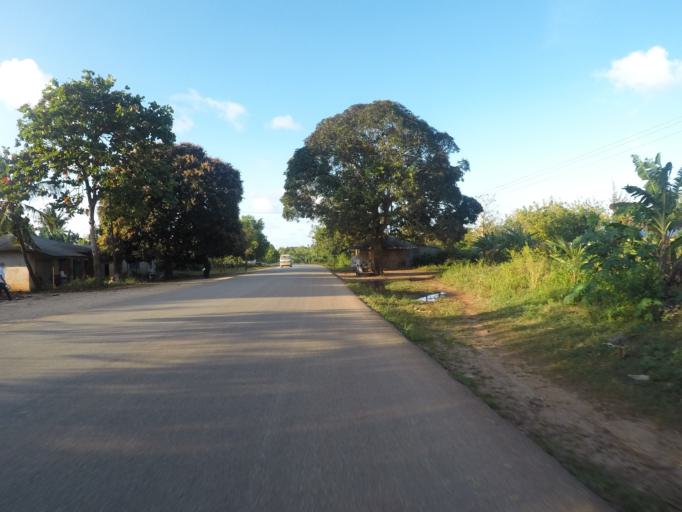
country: TZ
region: Zanzibar North
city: Kijini
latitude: -5.8121
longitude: 39.2938
